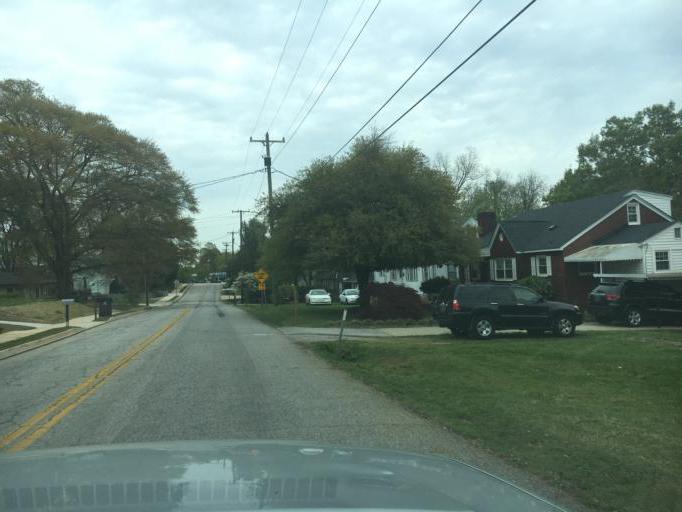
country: US
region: South Carolina
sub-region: Greenville County
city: Greenville
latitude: 34.8621
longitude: -82.3762
